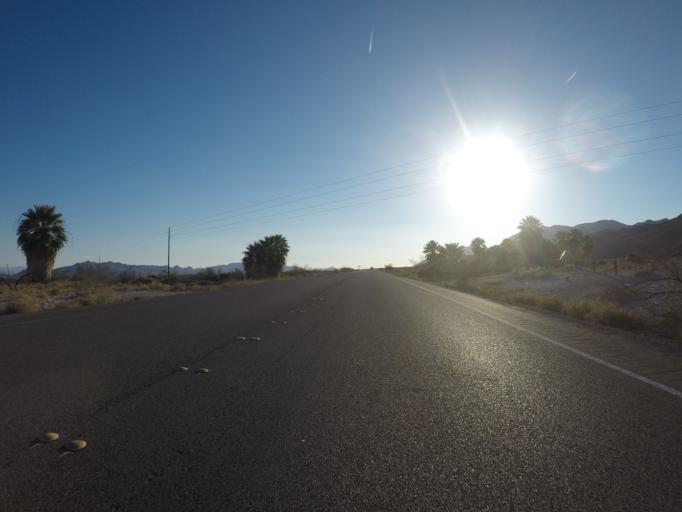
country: US
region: Nevada
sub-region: Clark County
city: Moapa Valley
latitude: 36.3904
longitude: -114.4280
